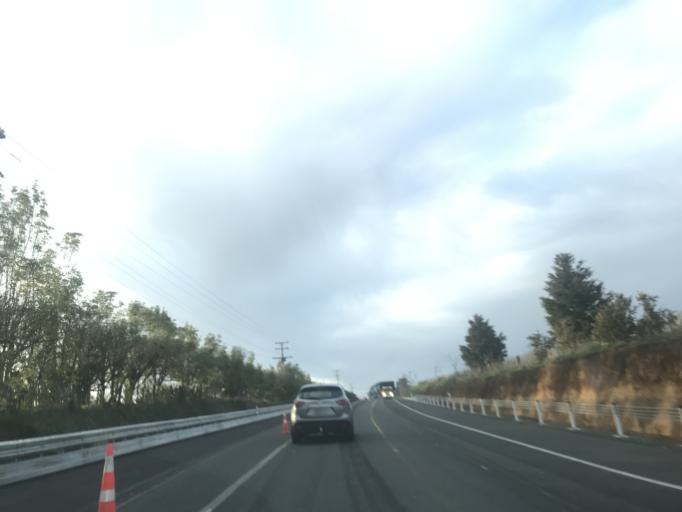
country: NZ
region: Bay of Plenty
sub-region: Western Bay of Plenty District
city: Waihi Beach
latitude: -37.4495
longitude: 175.8787
